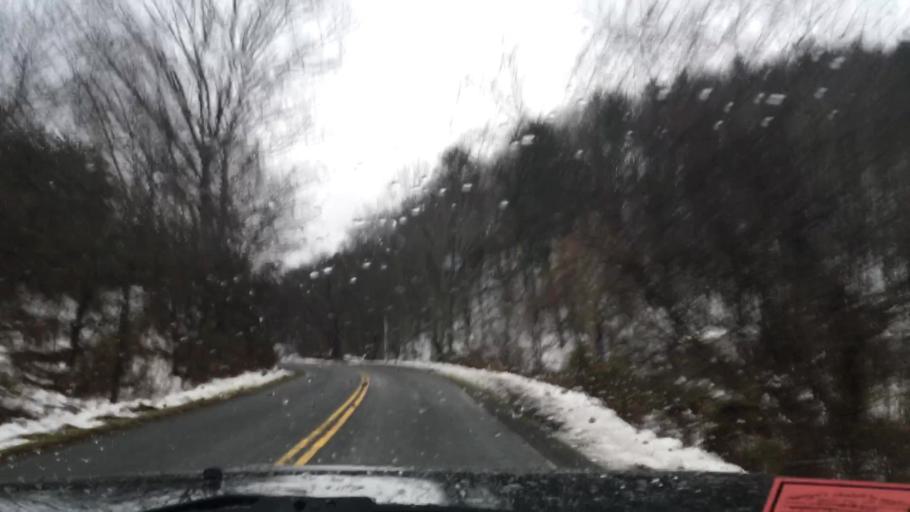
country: US
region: Virginia
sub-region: Pulaski County
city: Pulaski
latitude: 37.0133
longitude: -80.7024
